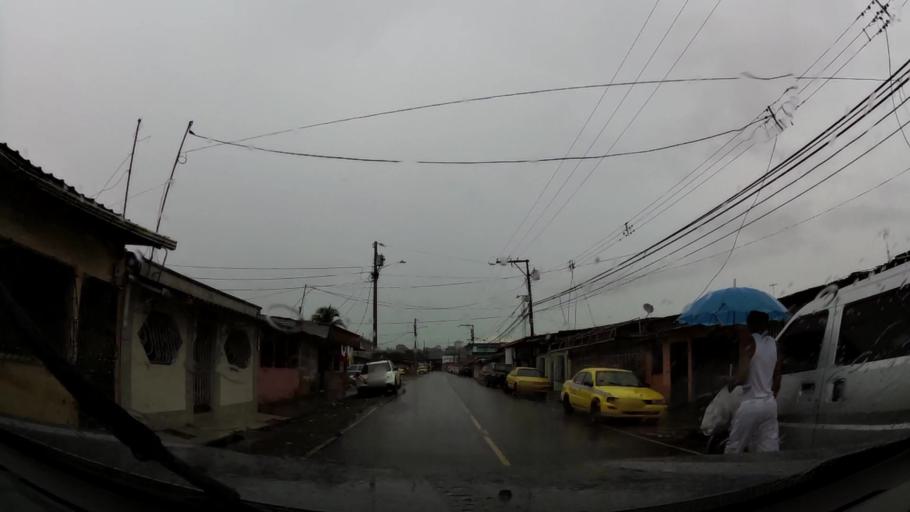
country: PA
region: Colon
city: Sabanitas
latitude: 9.3523
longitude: -79.8020
